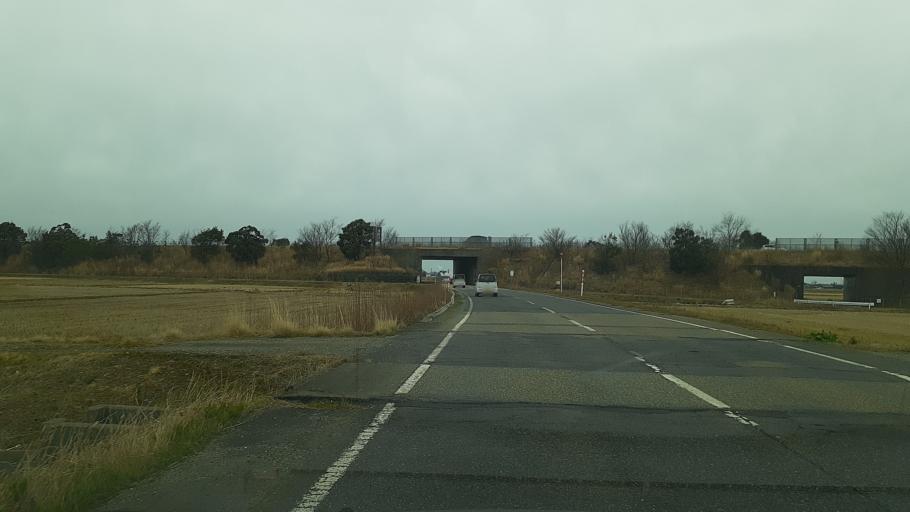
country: JP
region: Niigata
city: Niitsu-honcho
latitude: 37.8216
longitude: 139.0845
